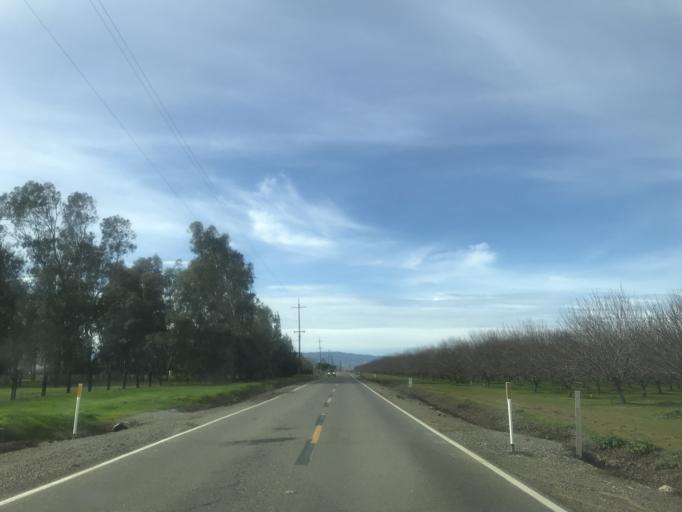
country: US
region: California
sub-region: Yolo County
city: Cottonwood
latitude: 38.6635
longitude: -121.8875
